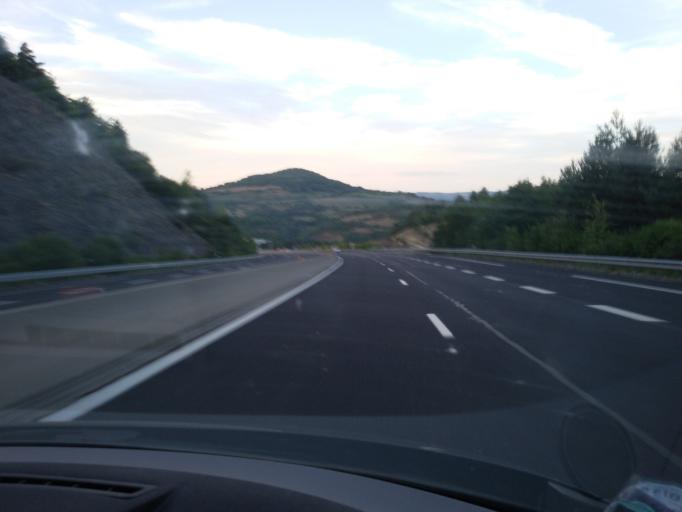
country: FR
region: Languedoc-Roussillon
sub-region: Departement de la Lozere
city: Chirac
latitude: 44.5039
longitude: 3.2434
